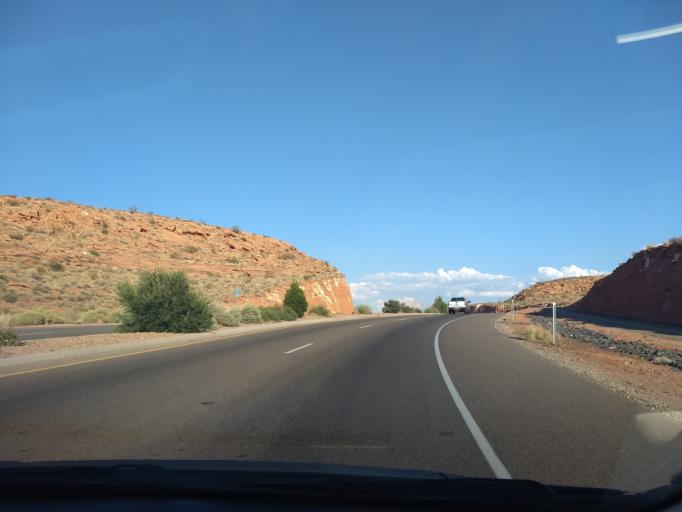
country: US
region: Utah
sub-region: Washington County
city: Saint George
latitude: 37.1356
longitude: -113.5982
